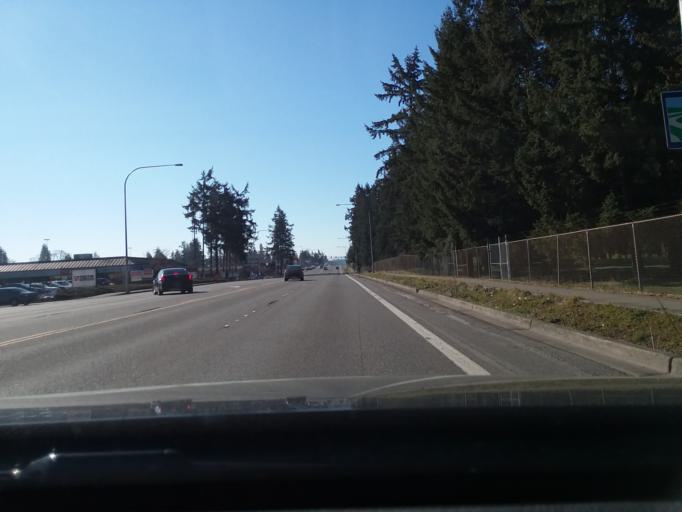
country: US
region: Washington
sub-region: Pierce County
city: Spanaway
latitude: 47.1154
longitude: -122.4350
